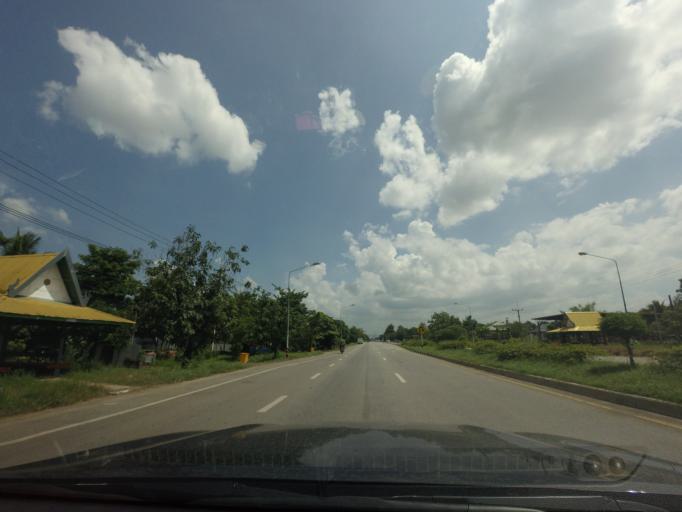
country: TH
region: Phetchabun
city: Phetchabun
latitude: 16.2565
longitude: 101.0593
